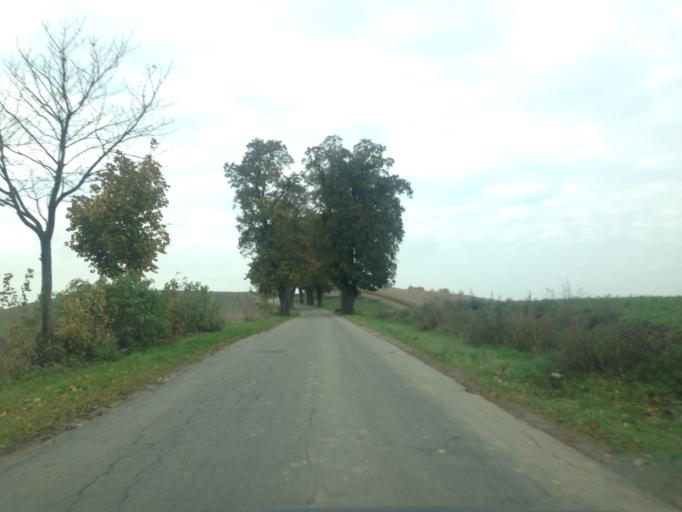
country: PL
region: Kujawsko-Pomorskie
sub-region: Powiat brodnicki
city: Brzozie
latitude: 53.2945
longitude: 19.6704
